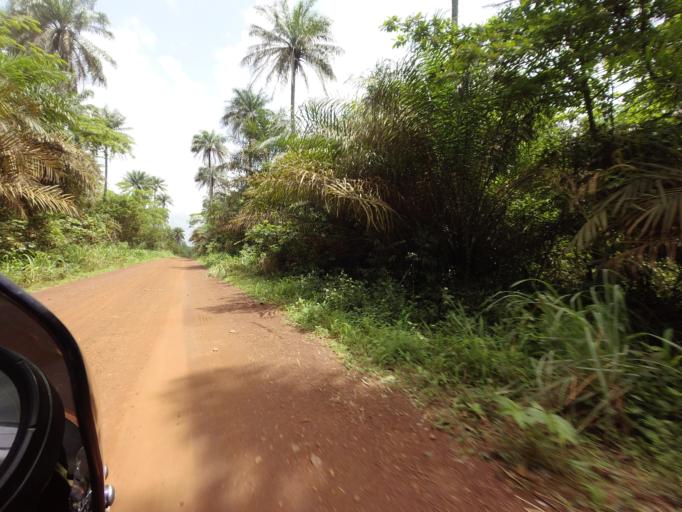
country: SL
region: Northern Province
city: Kambia
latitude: 9.1202
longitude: -12.9380
